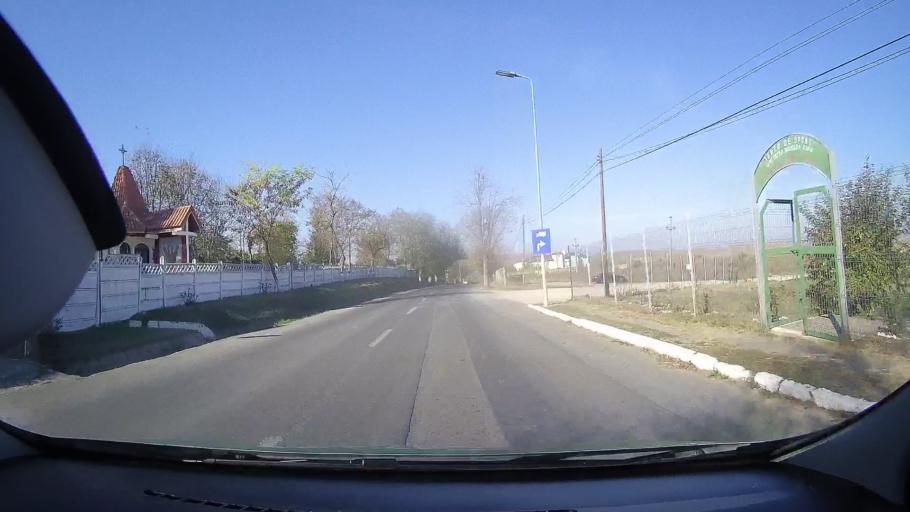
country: RO
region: Tulcea
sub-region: Oras Babadag
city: Babadag
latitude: 44.8859
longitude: 28.7355
